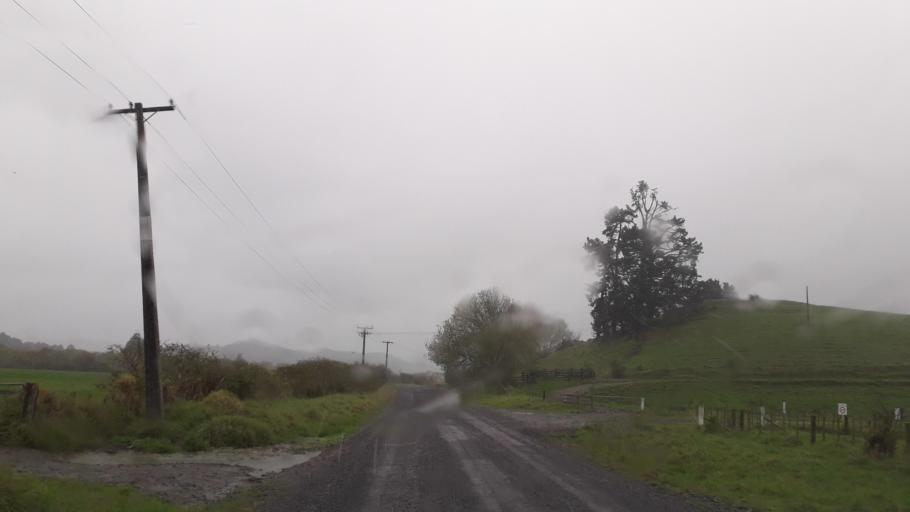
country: NZ
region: Northland
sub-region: Far North District
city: Waimate North
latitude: -35.4846
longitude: 173.6999
